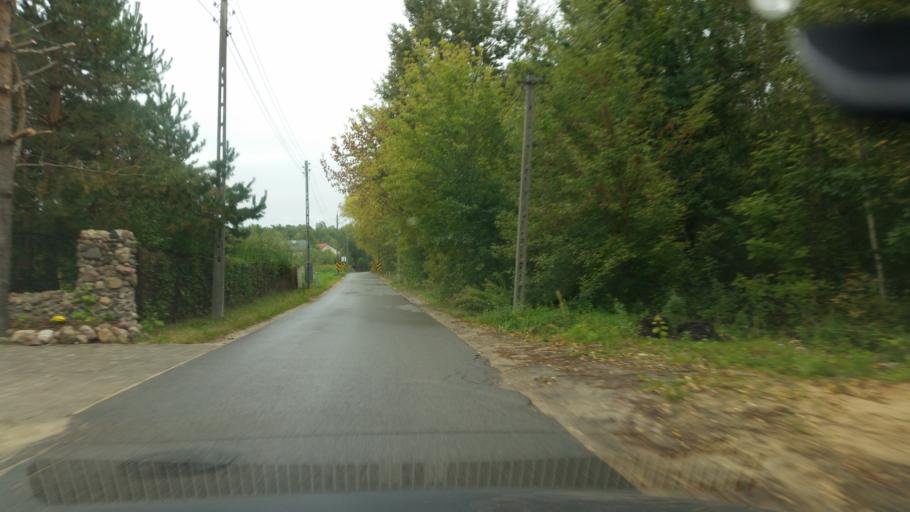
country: PL
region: Masovian Voivodeship
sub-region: Powiat piaseczynski
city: Jozefoslaw
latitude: 52.0913
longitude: 21.0774
